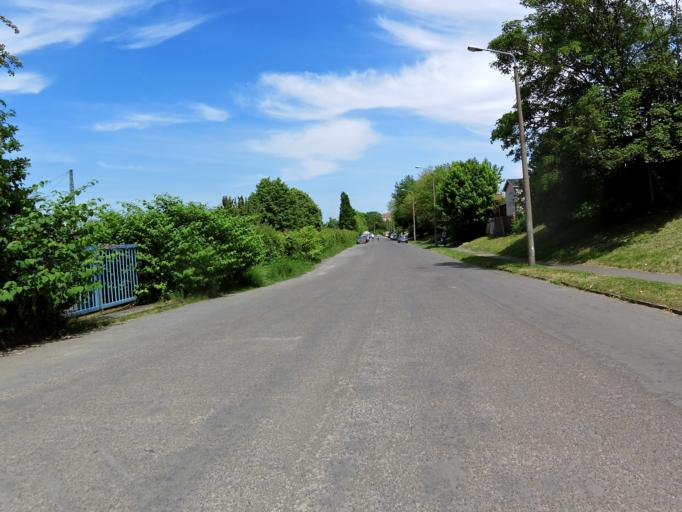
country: DE
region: Saxony
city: Leipzig
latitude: 51.3214
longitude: 12.4098
